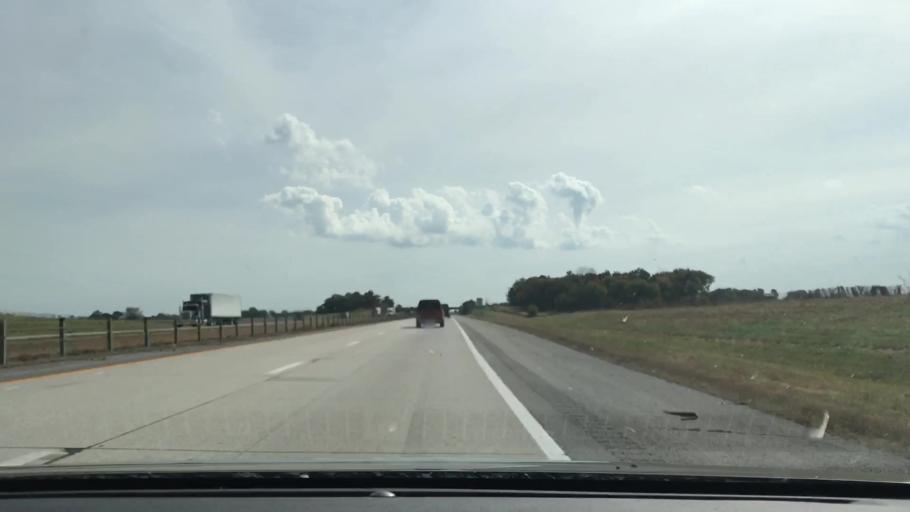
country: US
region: Kentucky
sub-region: Christian County
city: Hopkinsville
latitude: 36.8126
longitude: -87.6251
